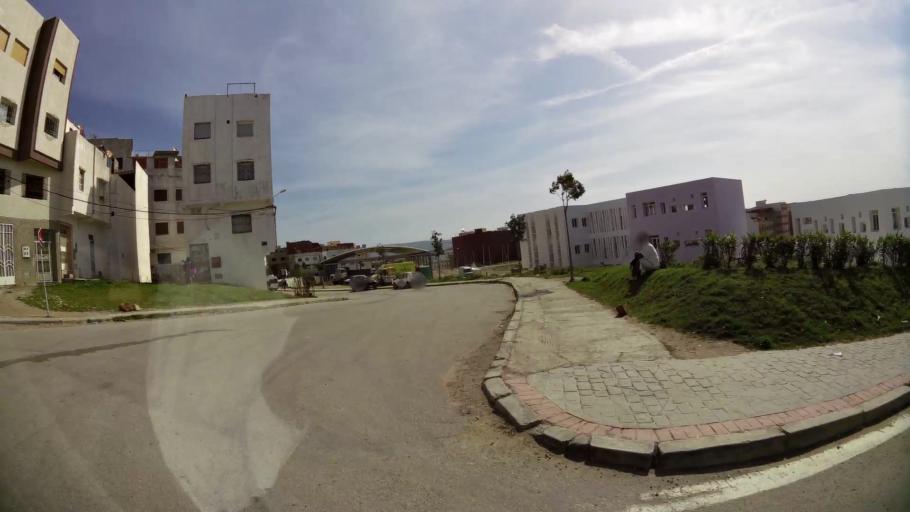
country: MA
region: Tanger-Tetouan
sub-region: Tanger-Assilah
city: Tangier
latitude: 35.7281
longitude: -5.8135
